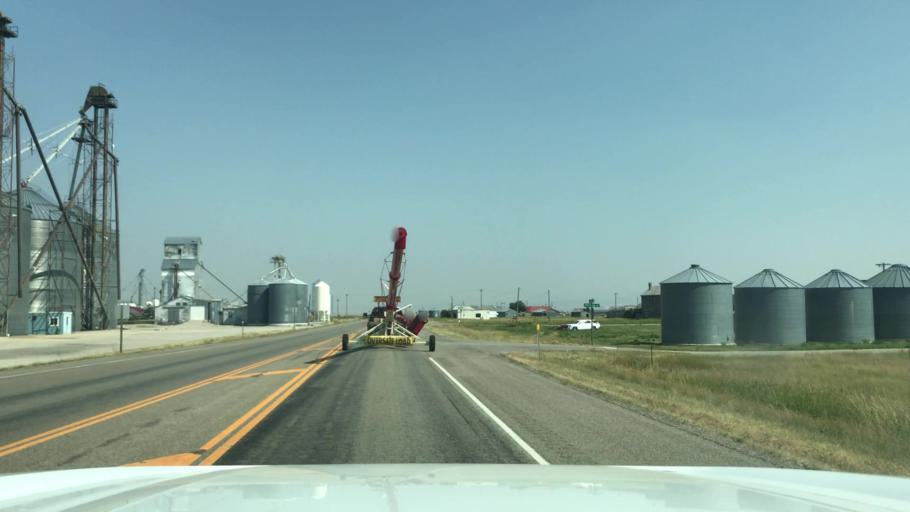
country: US
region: Montana
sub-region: Judith Basin County
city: Stanford
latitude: 47.0548
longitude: -109.9125
